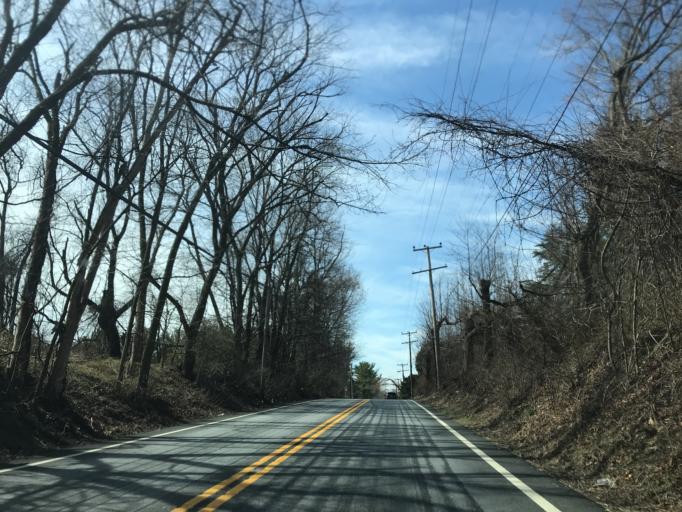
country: US
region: Maryland
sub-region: Montgomery County
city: Ashton-Sandy Spring
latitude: 39.1590
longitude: -76.9917
